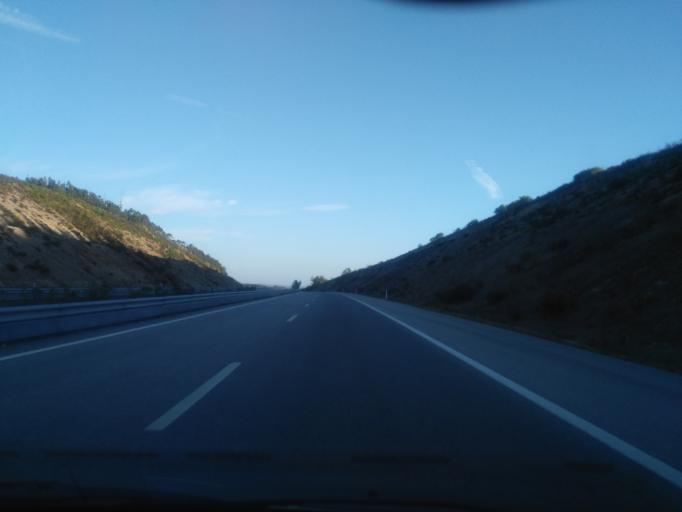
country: PT
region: Coimbra
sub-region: Figueira da Foz
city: Alhadas
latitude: 40.1886
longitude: -8.8117
